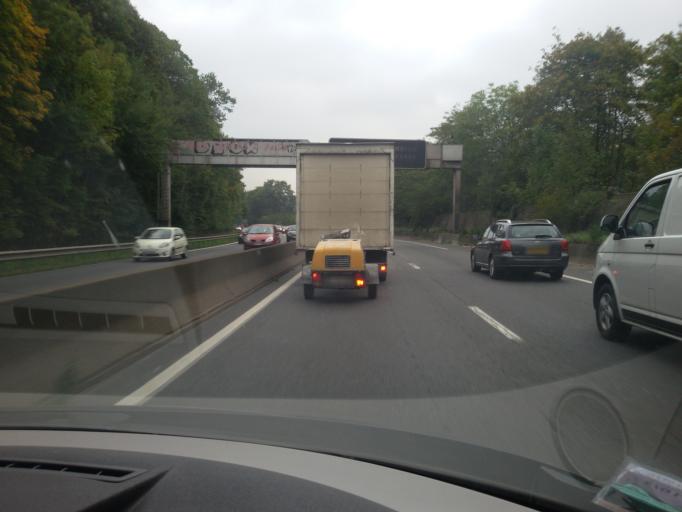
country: FR
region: Ile-de-France
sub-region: Departement de l'Essonne
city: Bievres
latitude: 48.7603
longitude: 2.2255
